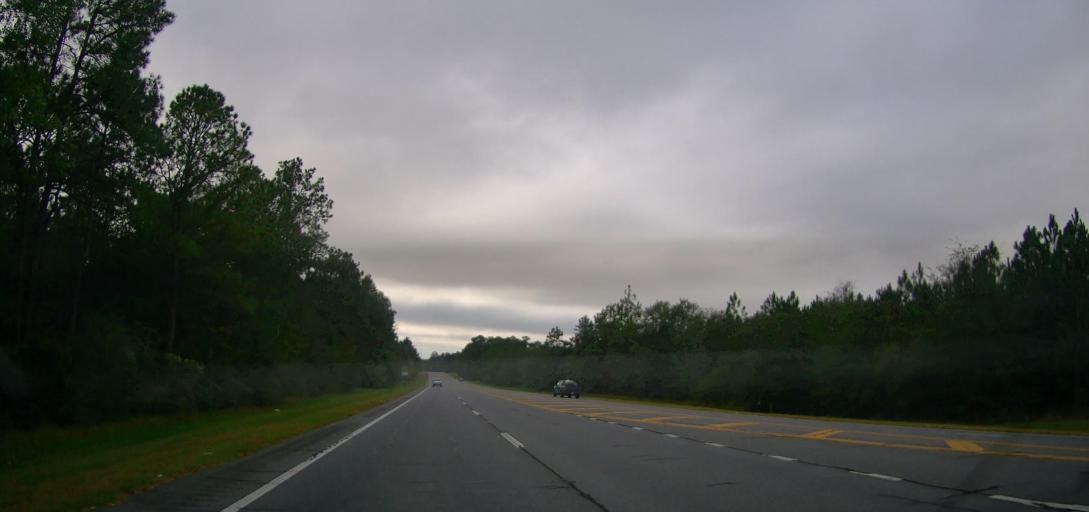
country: US
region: Georgia
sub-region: Colquitt County
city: Moultrie
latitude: 31.2511
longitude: -83.7166
